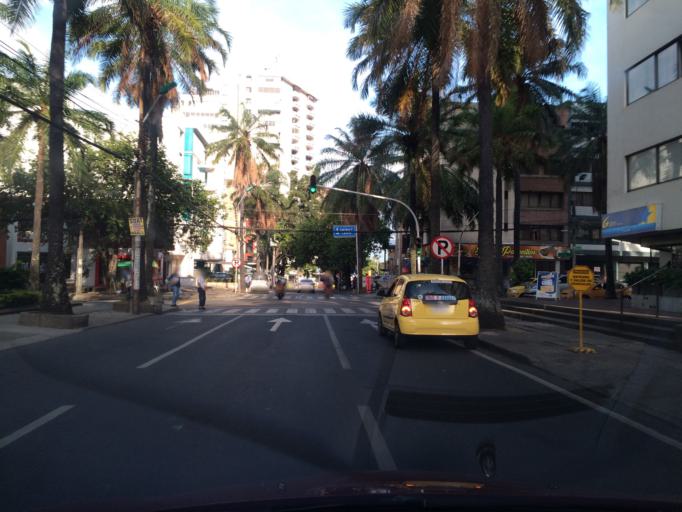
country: CO
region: Valle del Cauca
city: Cali
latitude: 3.4616
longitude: -76.5284
